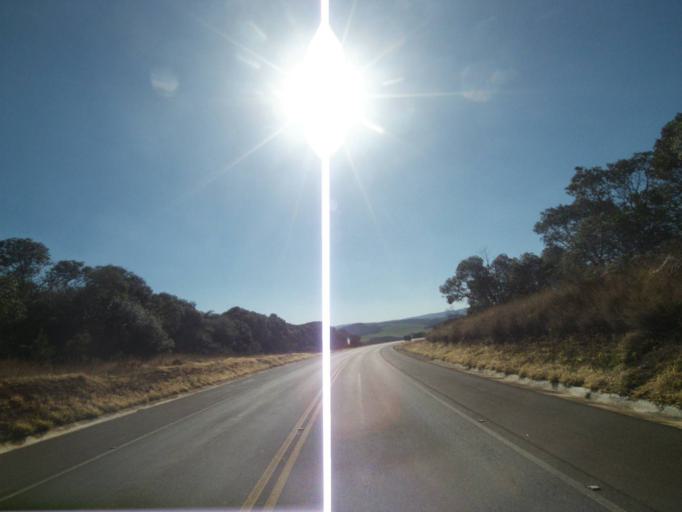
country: BR
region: Parana
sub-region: Tibagi
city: Tibagi
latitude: -24.6738
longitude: -50.4518
